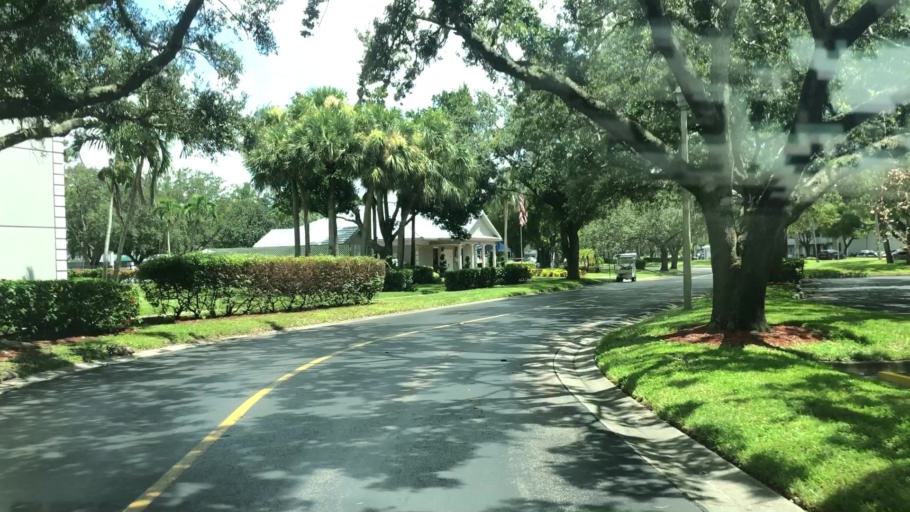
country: US
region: Florida
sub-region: Broward County
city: Pine Island Ridge
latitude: 26.0992
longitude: -80.2709
